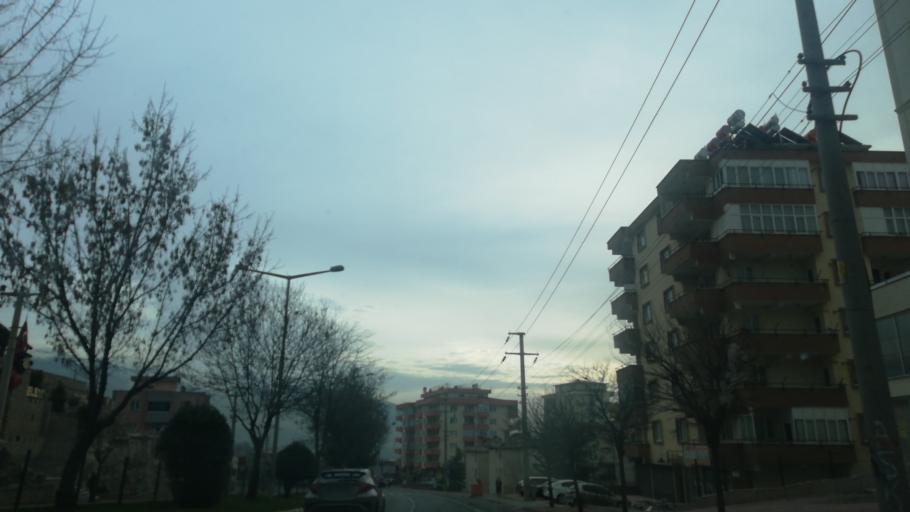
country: TR
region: Kahramanmaras
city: Kahramanmaras
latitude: 37.5929
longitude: 36.9023
